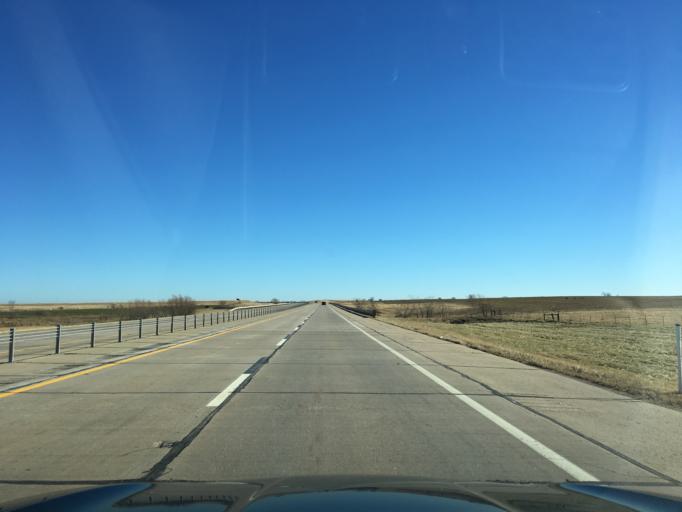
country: US
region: Oklahoma
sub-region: Noble County
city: Perry
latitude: 36.3964
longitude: -97.2278
